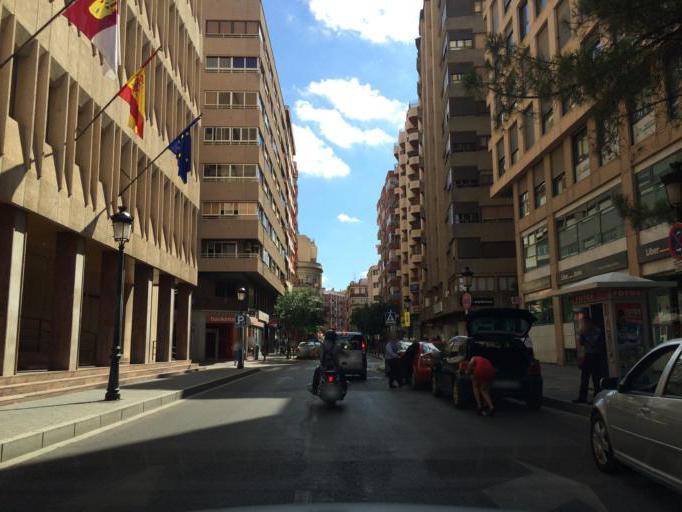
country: ES
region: Castille-La Mancha
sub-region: Provincia de Albacete
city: Albacete
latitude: 38.9948
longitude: -1.8535
